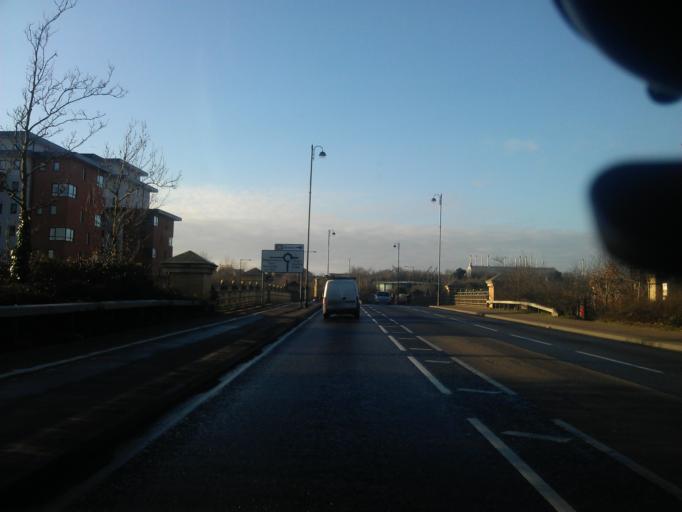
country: GB
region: England
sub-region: Essex
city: Colchester
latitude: 51.8803
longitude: 0.9293
